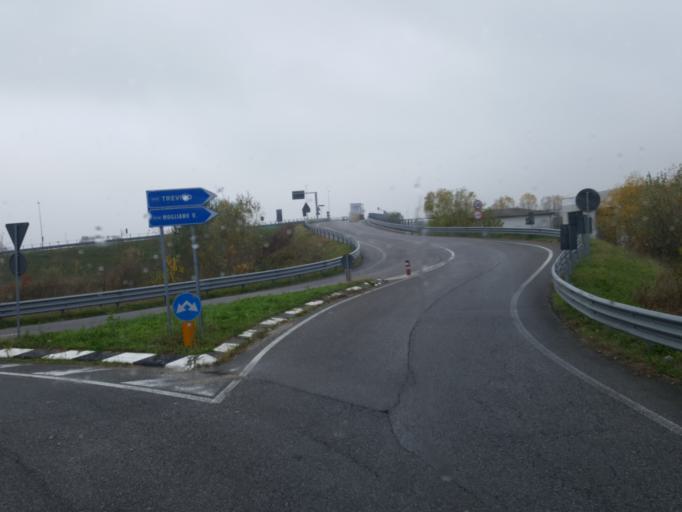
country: IT
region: Veneto
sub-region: Provincia di Venezia
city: Marcon-Gaggio-Colmello
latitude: 45.5680
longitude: 12.2783
